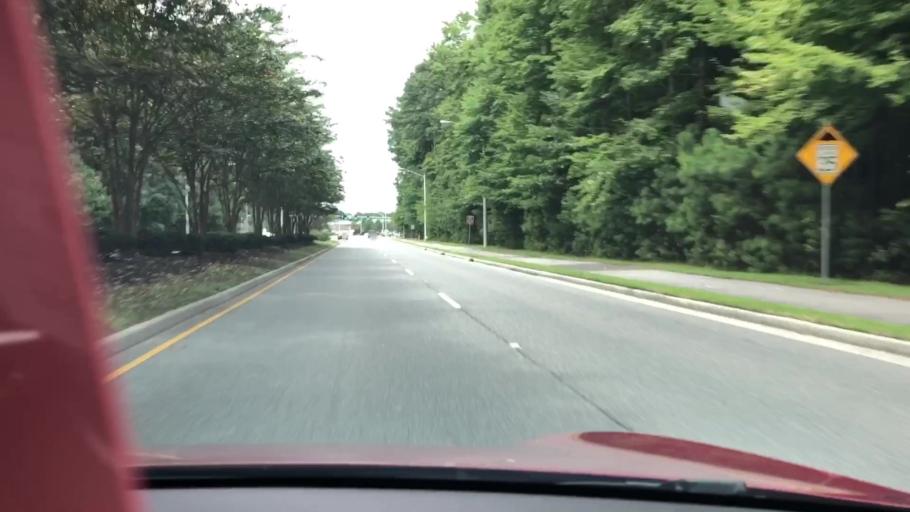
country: US
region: Virginia
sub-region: City of Virginia Beach
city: Virginia Beach
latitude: 36.8181
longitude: -75.9991
